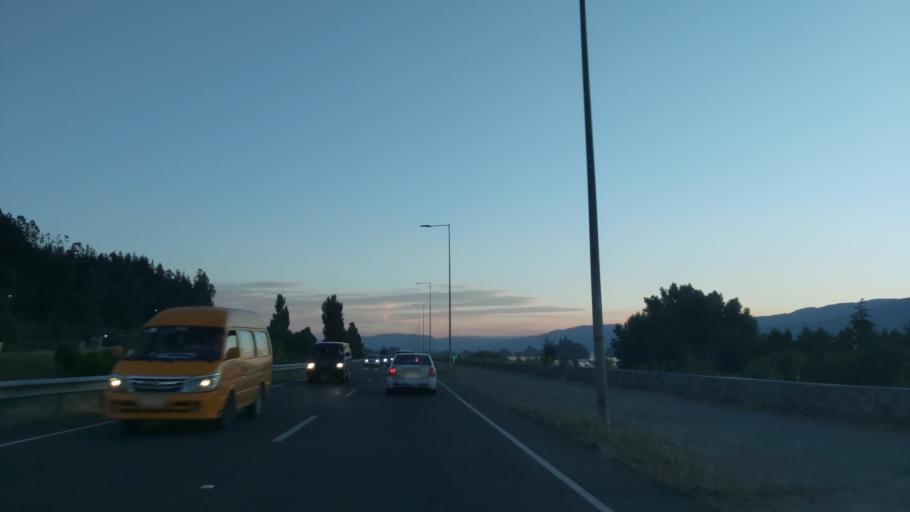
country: CL
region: Biobio
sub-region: Provincia de Concepcion
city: Chiguayante
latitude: -36.8831
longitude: -73.0386
